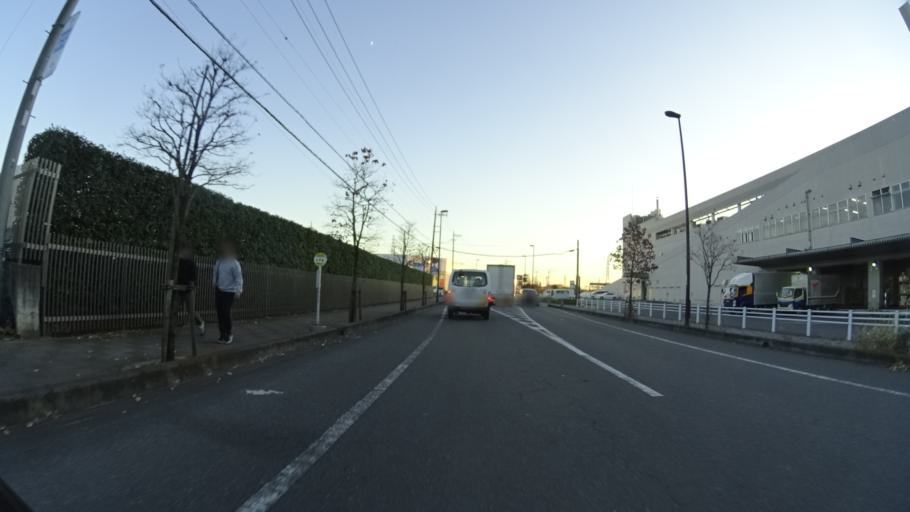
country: JP
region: Tochigi
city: Kaminokawa
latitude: 36.4909
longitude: 139.9081
